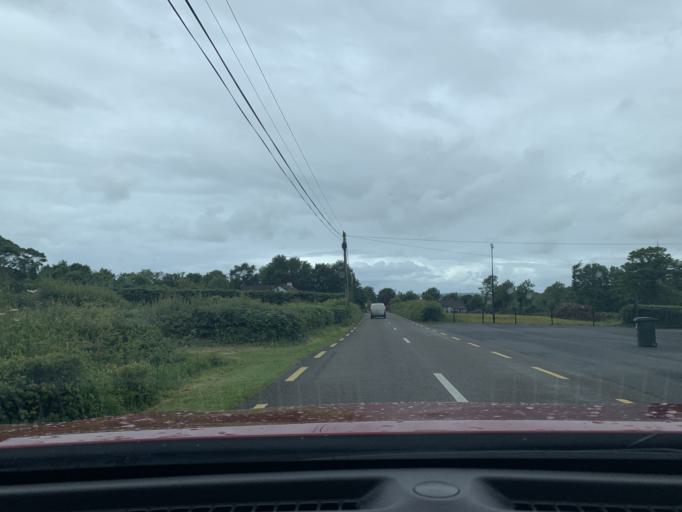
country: IE
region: Connaught
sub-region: Sligo
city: Sligo
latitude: 54.3153
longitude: -8.4759
